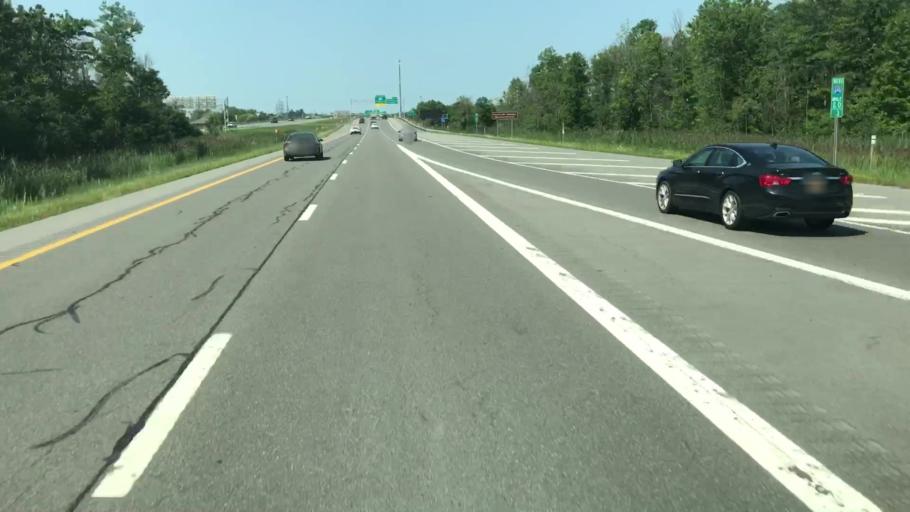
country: US
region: New York
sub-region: Onondaga County
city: East Syracuse
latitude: 43.0569
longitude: -76.0608
